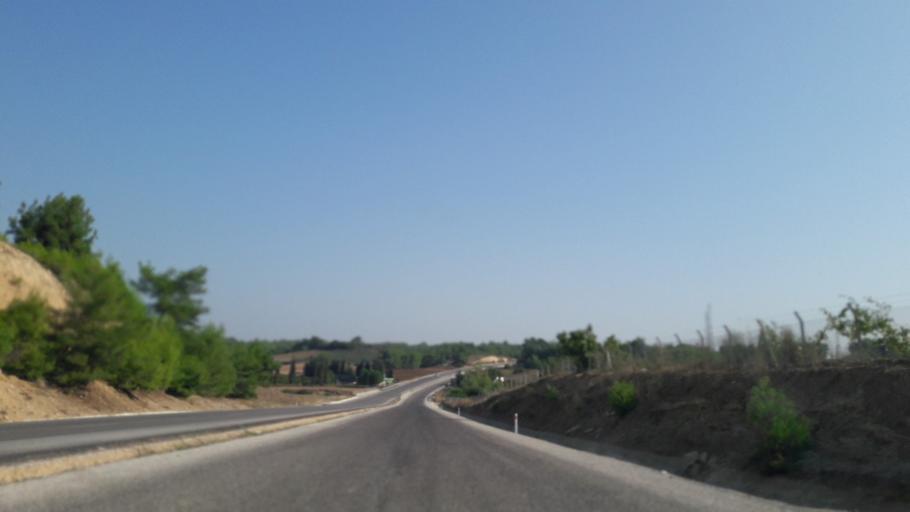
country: TR
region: Adana
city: Sagkaya
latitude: 37.1741
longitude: 35.5647
